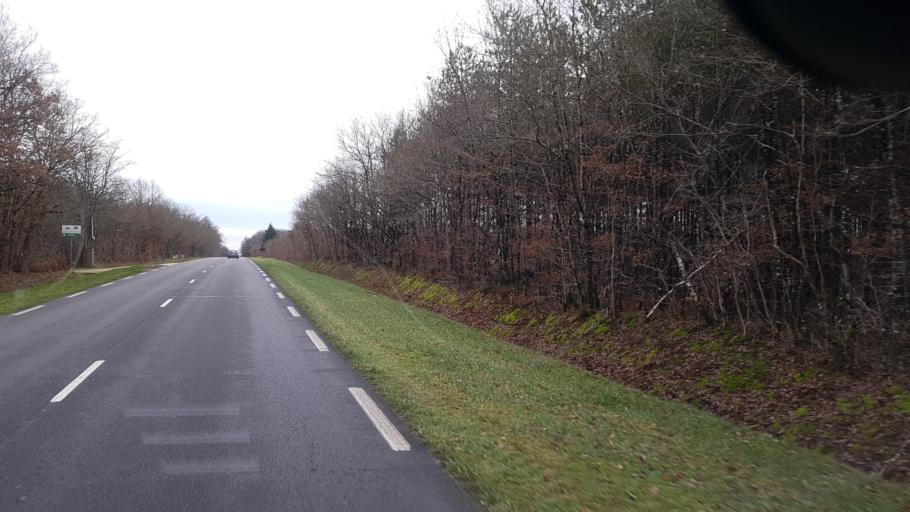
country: FR
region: Centre
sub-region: Departement du Loir-et-Cher
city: Lamotte-Beuvron
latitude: 47.6240
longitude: 2.0104
